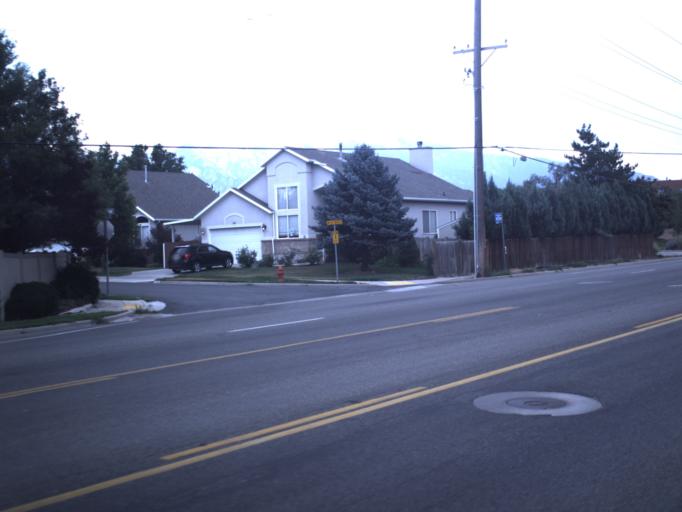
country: US
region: Utah
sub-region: Salt Lake County
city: Murray
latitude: 40.6445
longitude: -111.8661
